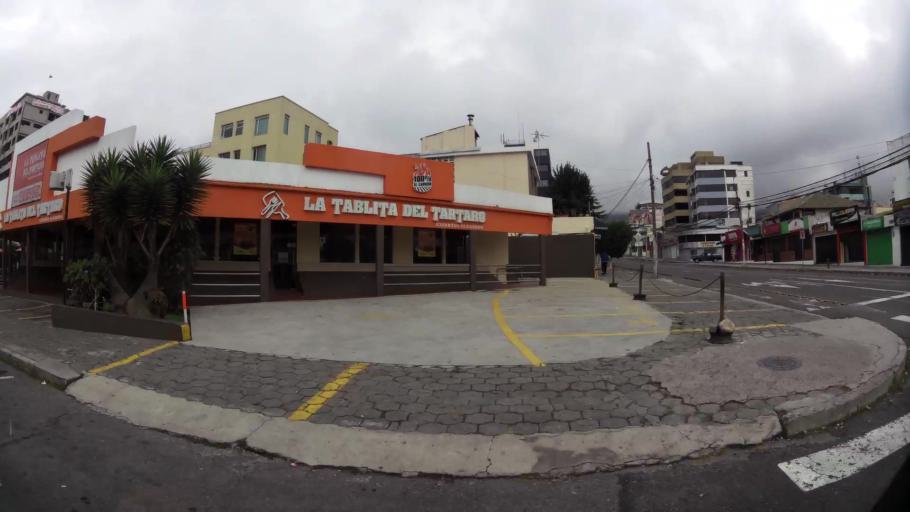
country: EC
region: Pichincha
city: Quito
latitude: -0.1899
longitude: -78.4889
